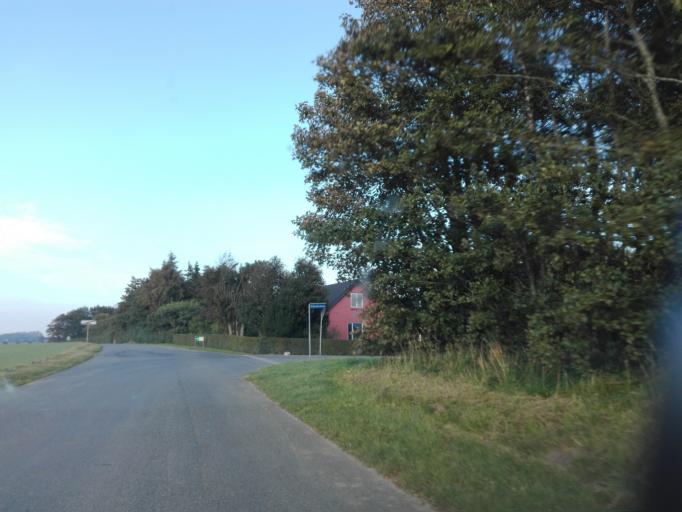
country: DK
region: Central Jutland
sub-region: Odder Kommune
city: Odder
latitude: 55.9470
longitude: 10.1952
